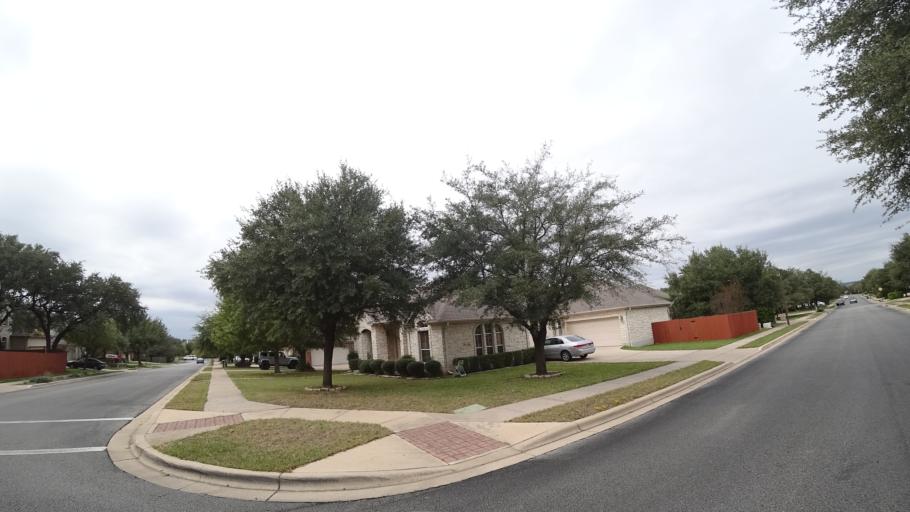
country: US
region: Texas
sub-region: Williamson County
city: Brushy Creek
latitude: 30.5122
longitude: -97.7472
